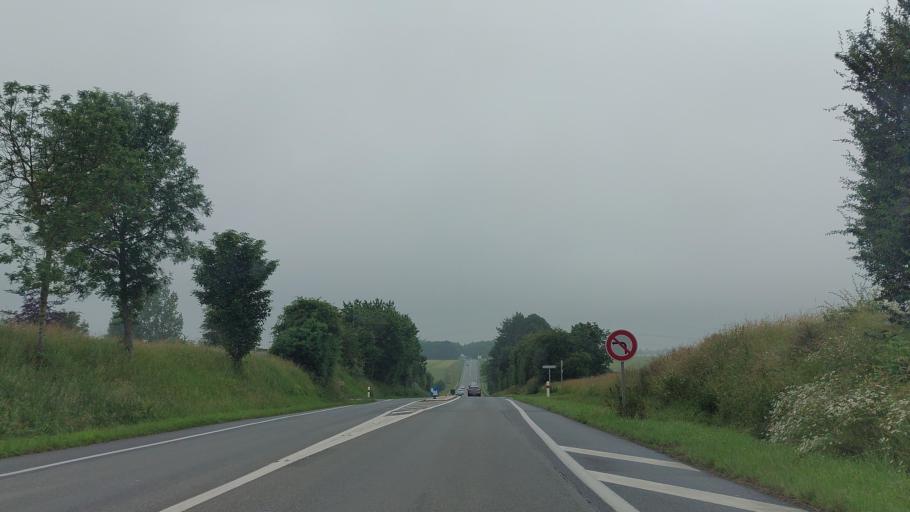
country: FR
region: Picardie
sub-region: Departement de la Somme
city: Fressenneville
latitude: 50.0742
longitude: 1.5728
